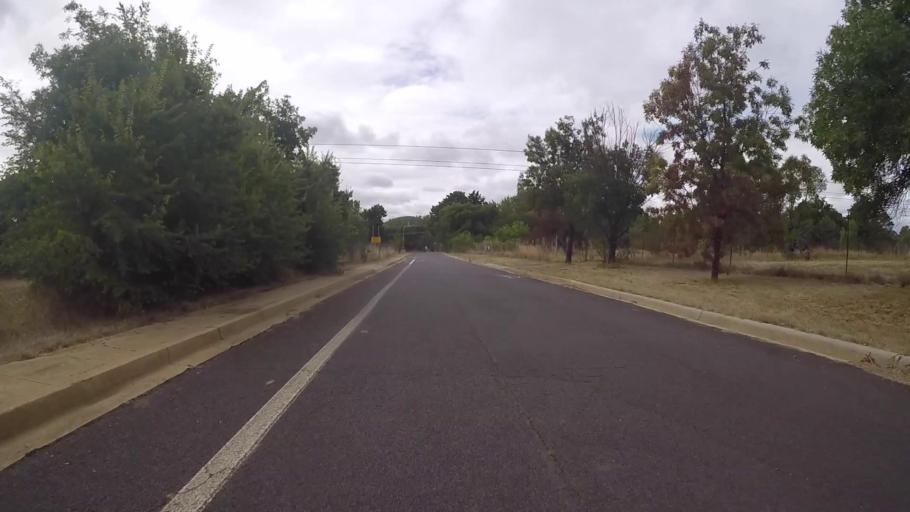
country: AU
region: Australian Capital Territory
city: Forrest
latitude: -35.3158
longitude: 149.1533
